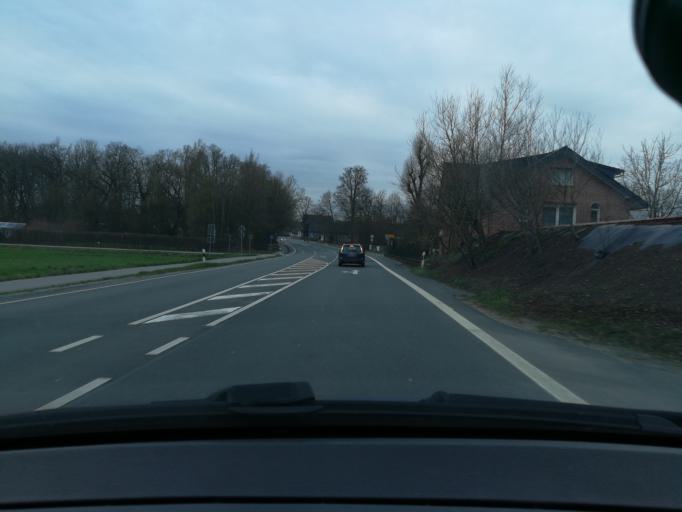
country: DE
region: North Rhine-Westphalia
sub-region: Regierungsbezirk Detmold
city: Oerlinghausen
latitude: 51.9293
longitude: 8.6133
